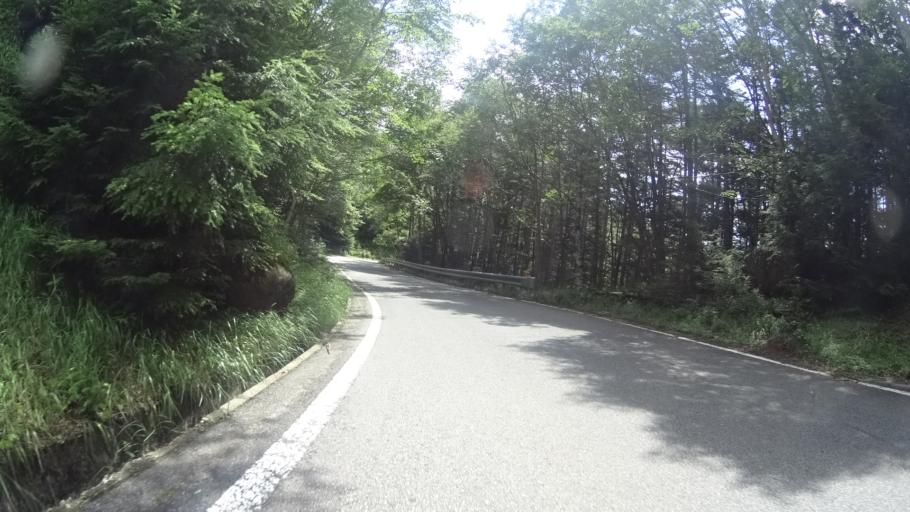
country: JP
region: Yamanashi
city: Enzan
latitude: 35.8588
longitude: 138.6484
